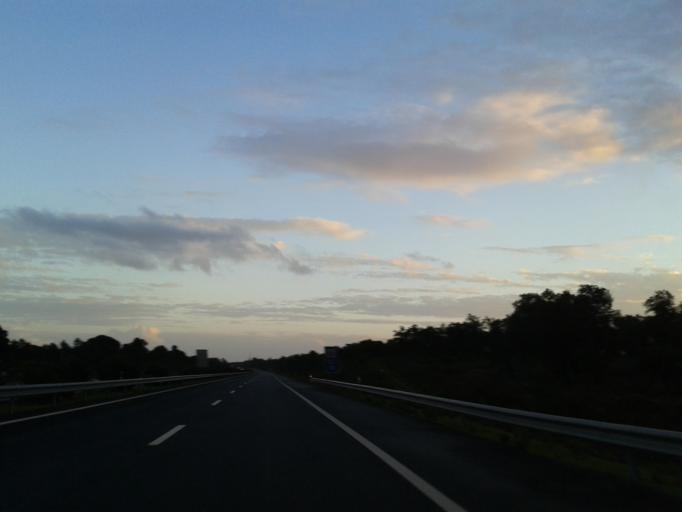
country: PT
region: Santarem
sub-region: Benavente
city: Poceirao
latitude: 38.8277
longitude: -8.7175
